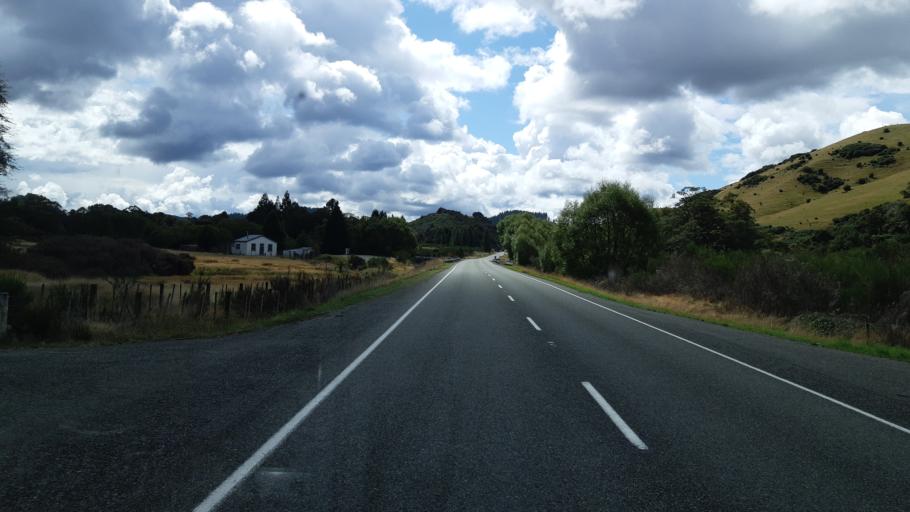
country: NZ
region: Tasman
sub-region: Tasman District
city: Wakefield
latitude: -41.6503
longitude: 172.6489
